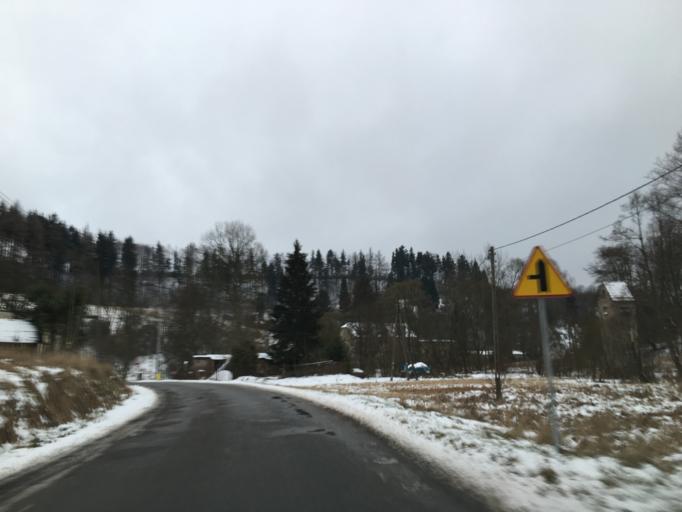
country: CZ
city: Radvanice
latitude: 50.6317
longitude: 16.0439
